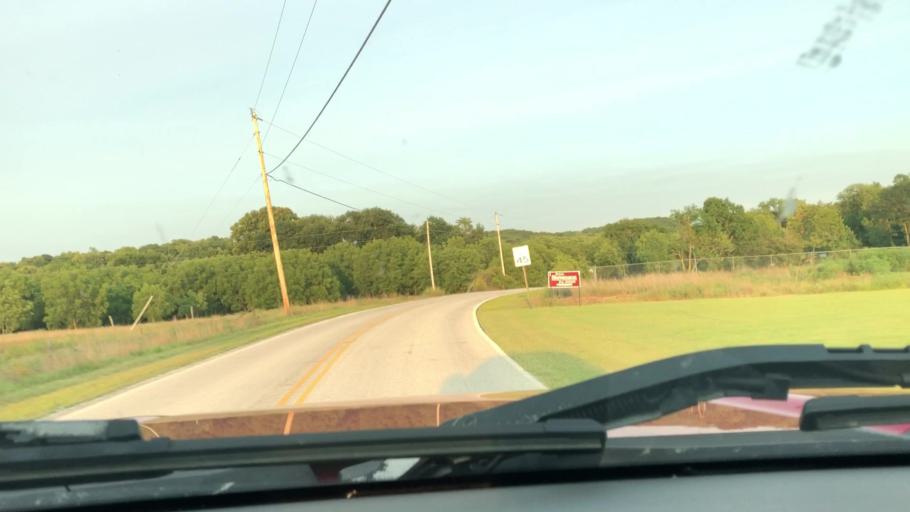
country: US
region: Missouri
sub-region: Jasper County
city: Joplin
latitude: 37.0210
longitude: -94.5115
